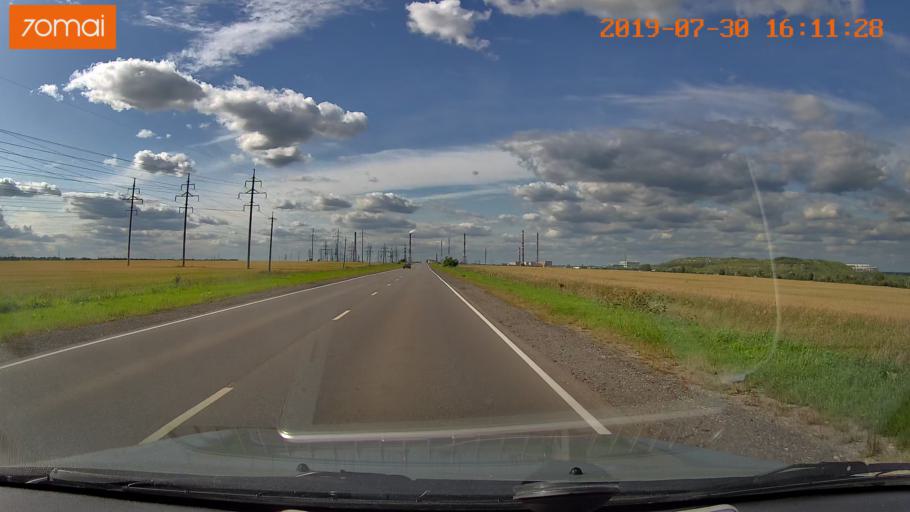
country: RU
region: Moskovskaya
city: Lopatinskiy
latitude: 55.2766
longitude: 38.7103
